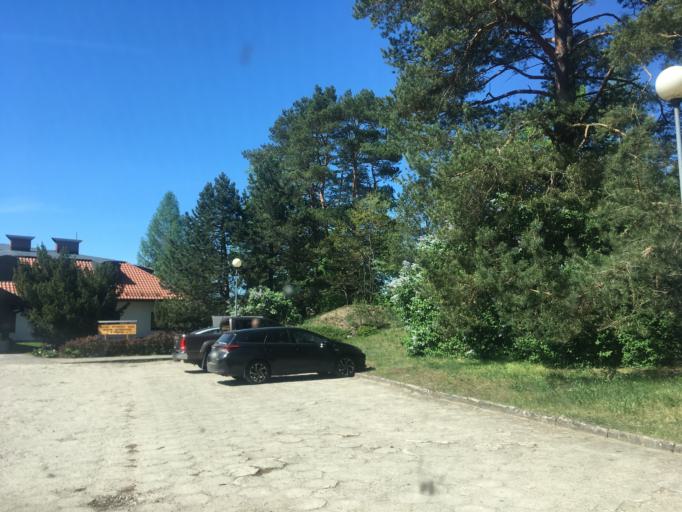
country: PL
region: Warmian-Masurian Voivodeship
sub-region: Powiat mragowski
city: Mikolajki
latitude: 53.7553
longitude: 21.6096
